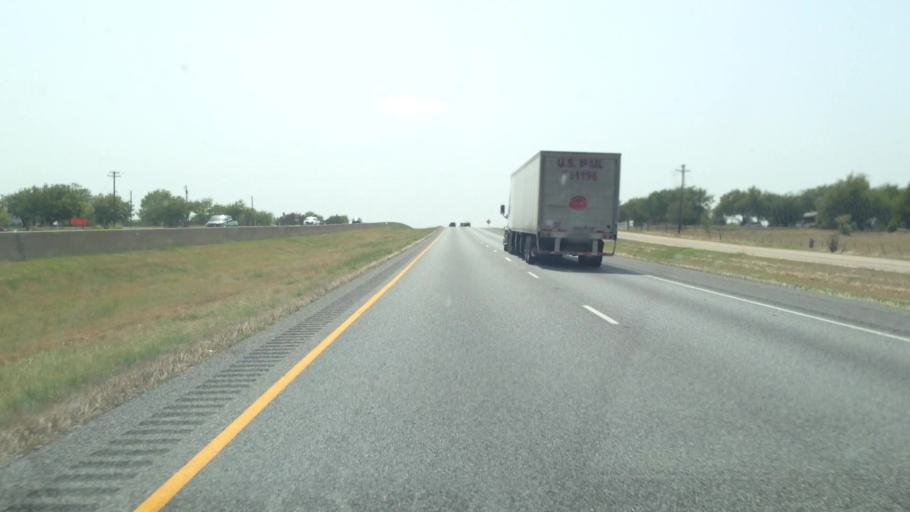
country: US
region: Texas
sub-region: Hunt County
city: Commerce
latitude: 33.1318
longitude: -95.9342
